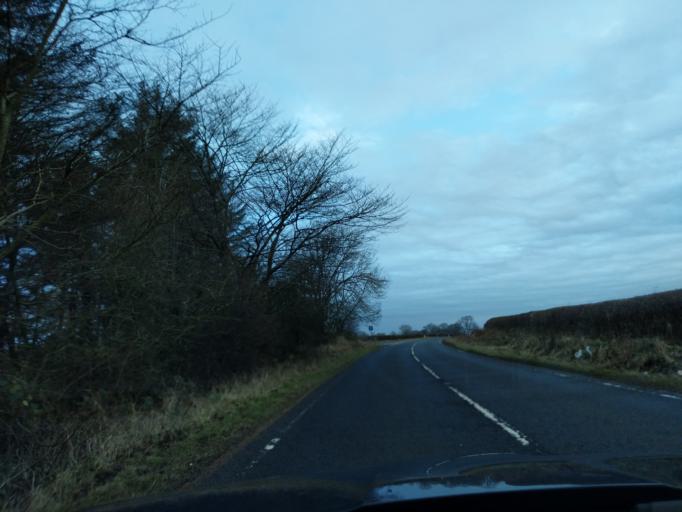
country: GB
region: England
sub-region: Northumberland
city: Rothley
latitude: 55.1230
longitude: -1.9212
